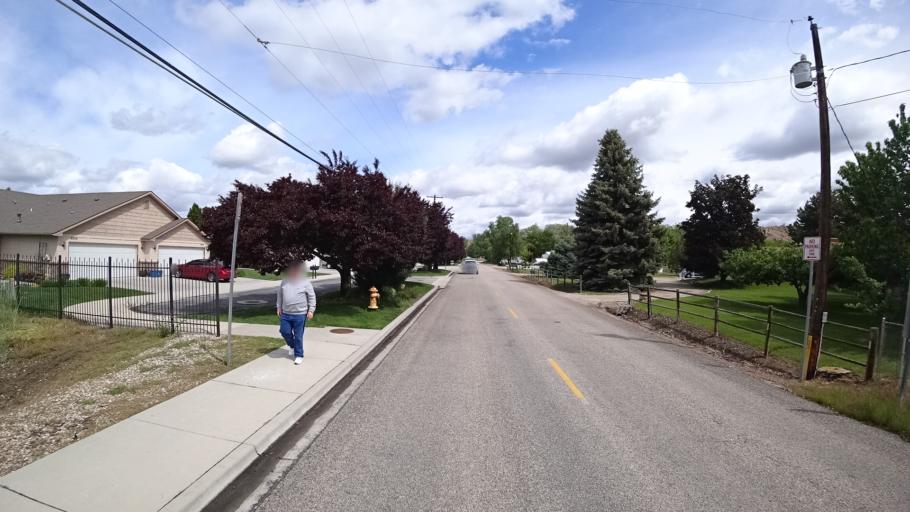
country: US
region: Idaho
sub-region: Ada County
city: Eagle
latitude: 43.6849
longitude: -116.3015
